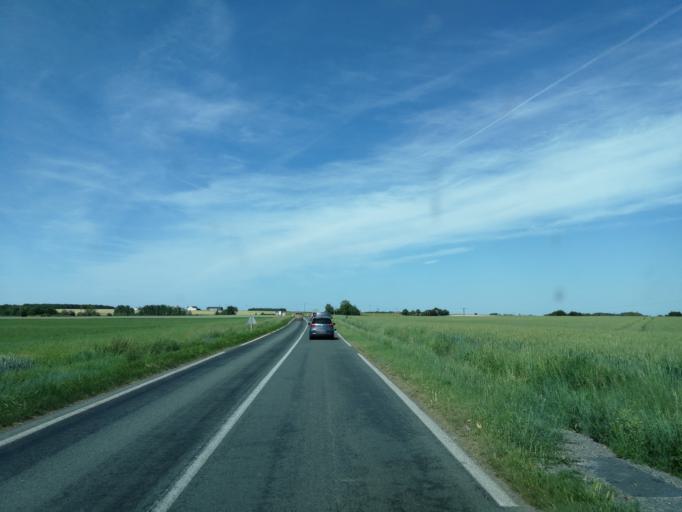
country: FR
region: Poitou-Charentes
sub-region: Departement de la Vienne
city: Loudun
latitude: 47.0207
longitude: 0.1027
